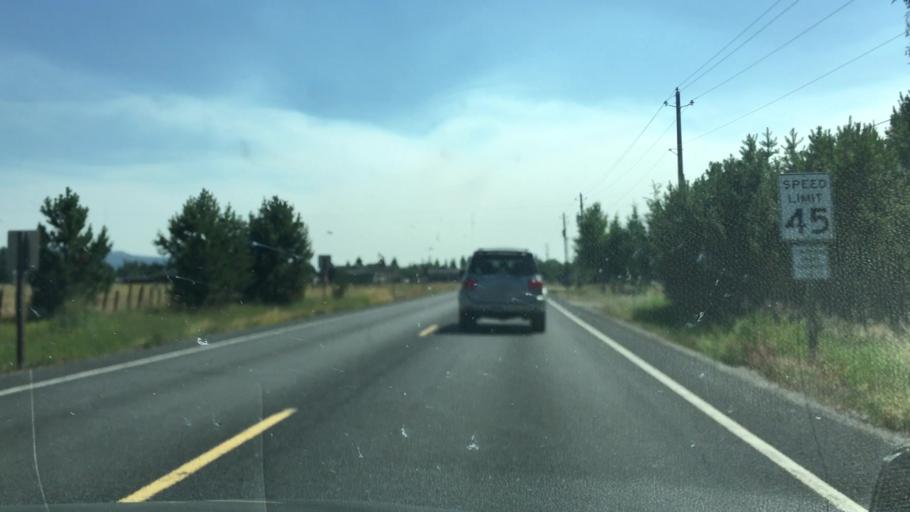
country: US
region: Idaho
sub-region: Valley County
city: McCall
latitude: 44.7391
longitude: -116.0783
